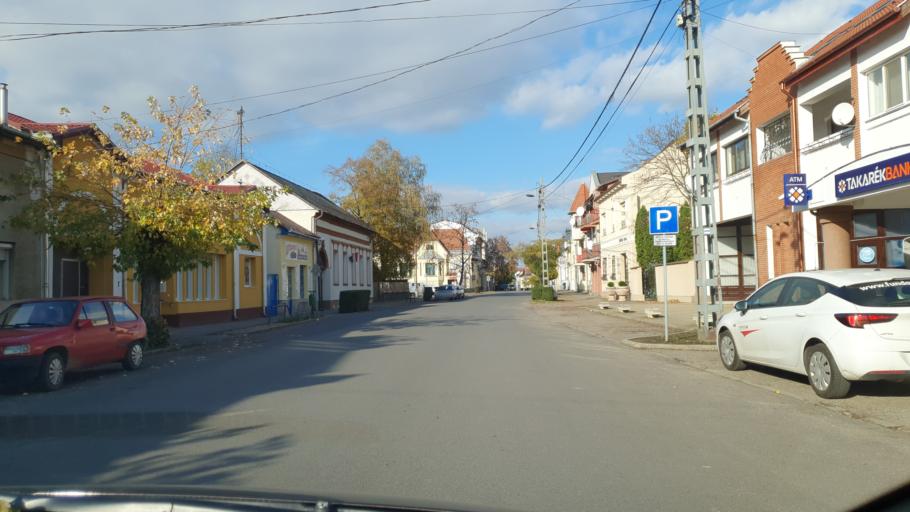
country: HU
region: Szabolcs-Szatmar-Bereg
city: Kisvarda
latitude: 48.2204
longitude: 22.0800
